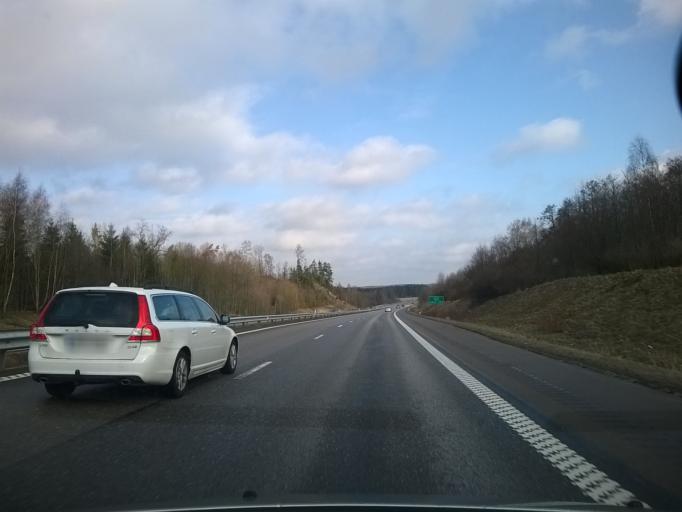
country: SE
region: Vaestra Goetaland
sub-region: Uddevalla Kommun
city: Uddevalla
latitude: 58.3004
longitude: 11.8605
